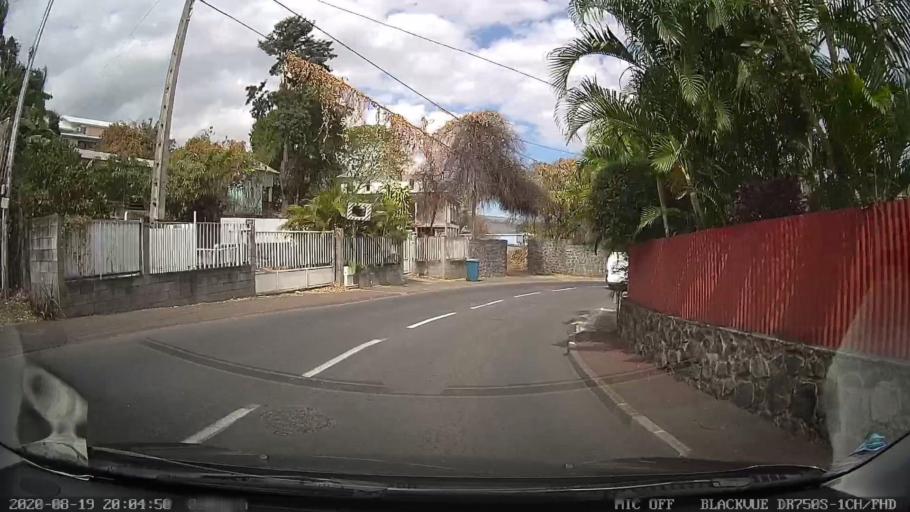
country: RE
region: Reunion
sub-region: Reunion
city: La Possession
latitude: -20.9522
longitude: 55.3416
